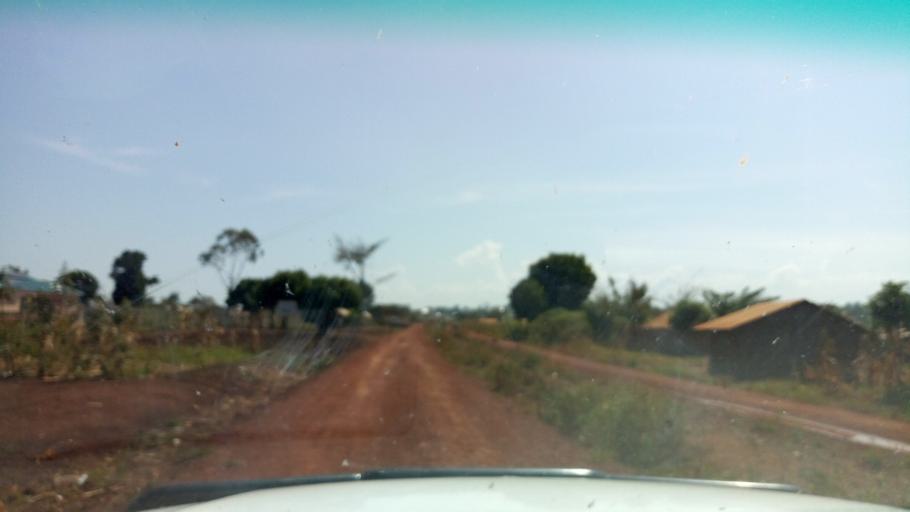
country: UG
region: Western Region
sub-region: Kiryandongo District
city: Kiryandongo
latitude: 1.9491
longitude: 32.1548
